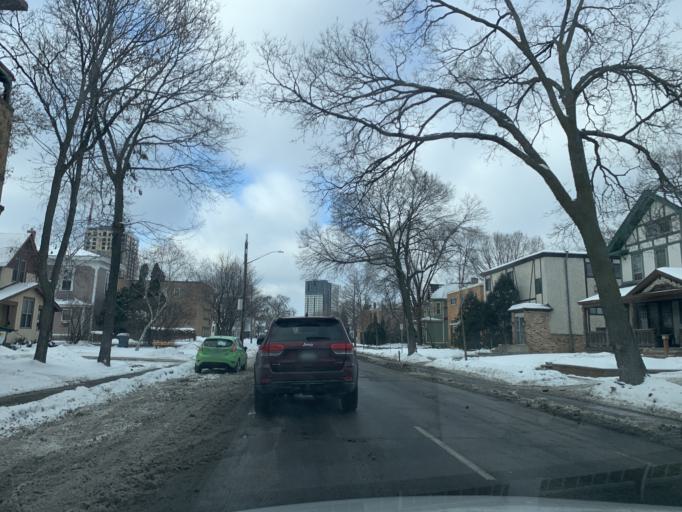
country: US
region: Minnesota
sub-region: Hennepin County
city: Minneapolis
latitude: 44.9850
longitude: -93.2471
